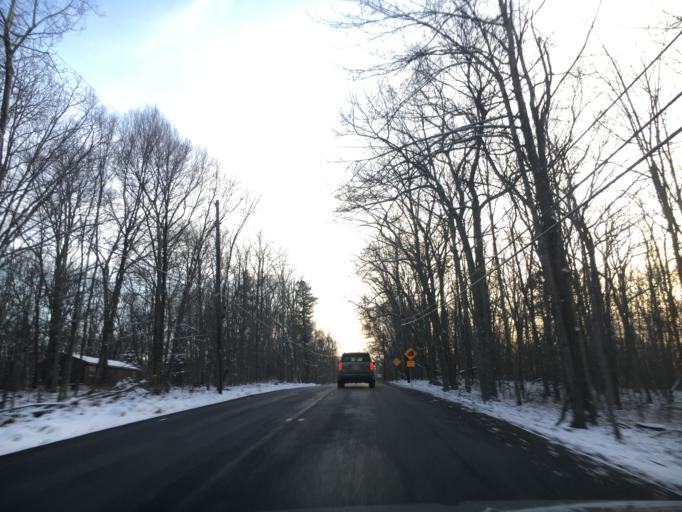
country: US
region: Pennsylvania
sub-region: Pike County
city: Saw Creek
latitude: 41.1315
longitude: -75.0873
